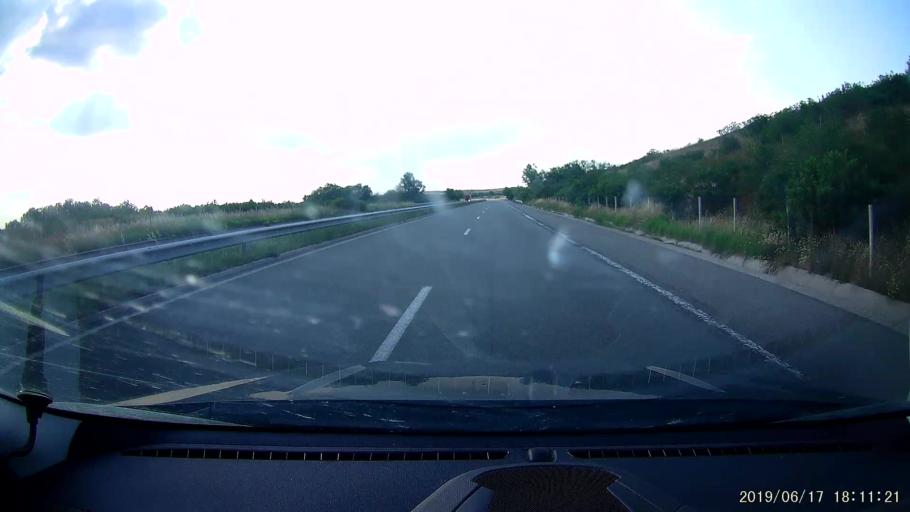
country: BG
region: Khaskovo
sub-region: Obshtina Lyubimets
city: Lyubimets
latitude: 41.8828
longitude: 26.0529
